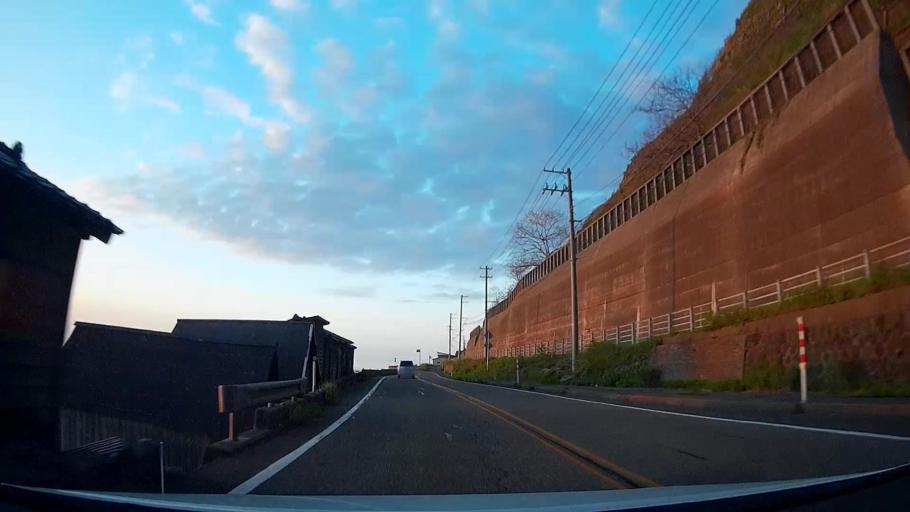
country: JP
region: Niigata
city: Joetsu
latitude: 37.1395
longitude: 138.0593
